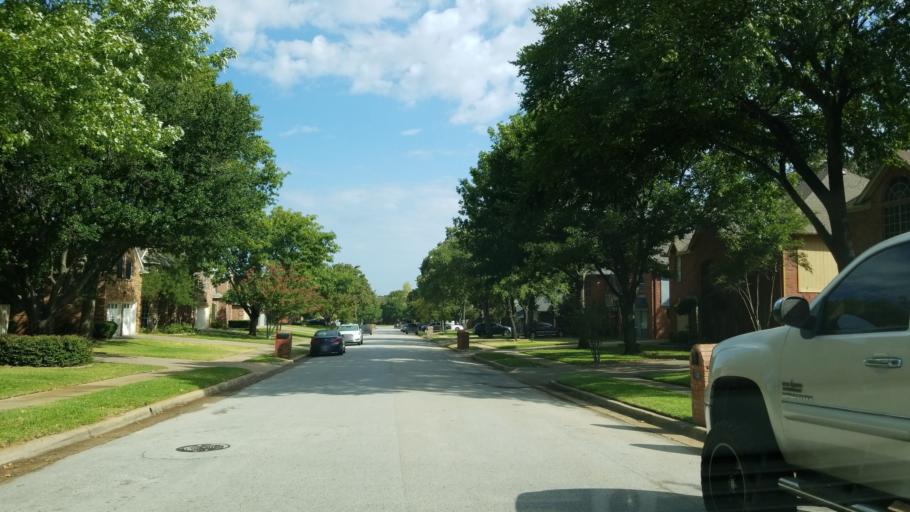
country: US
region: Texas
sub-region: Tarrant County
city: Grapevine
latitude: 32.8902
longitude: -97.0871
